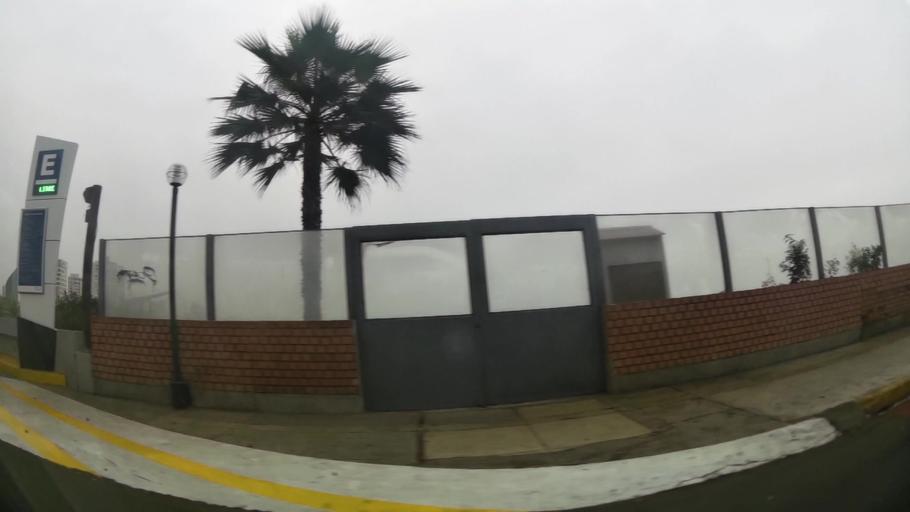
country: PE
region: Lima
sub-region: Lima
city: San Isidro
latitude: -12.1311
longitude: -77.0319
